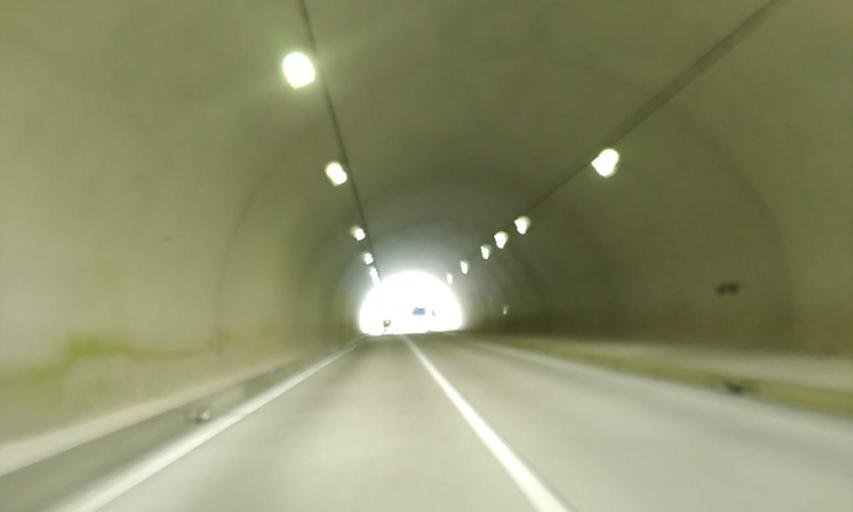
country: JP
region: Mie
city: Ise
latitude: 34.2857
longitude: 136.5568
